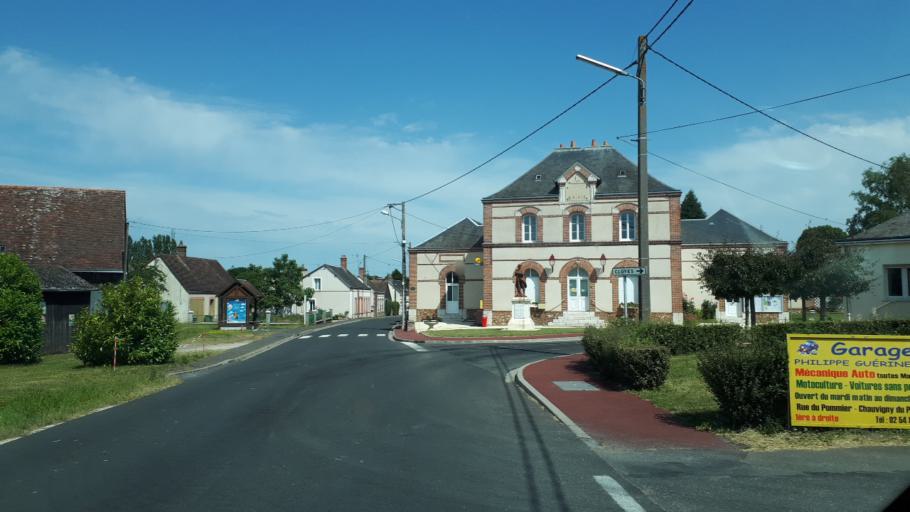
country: FR
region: Centre
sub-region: Departement du Loir-et-Cher
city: La Ville-aux-Clercs
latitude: 47.9567
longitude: 1.0801
